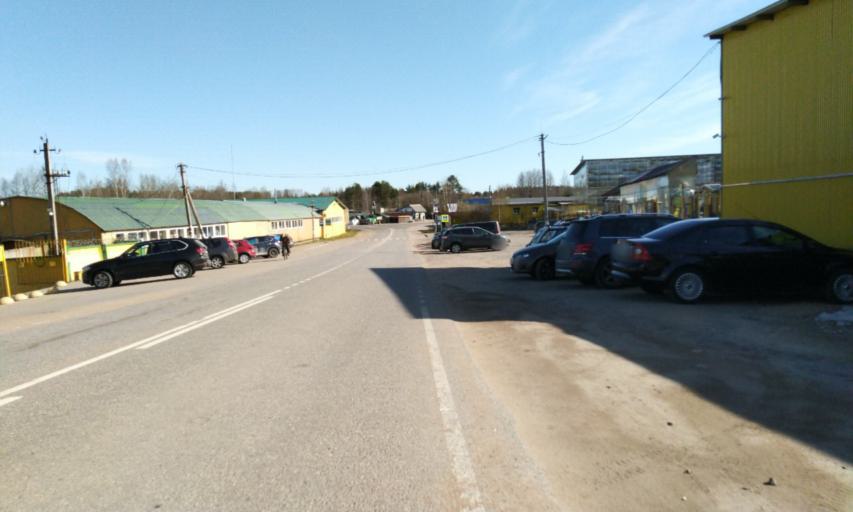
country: RU
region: Leningrad
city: Garbolovo
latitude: 60.3291
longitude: 30.4248
